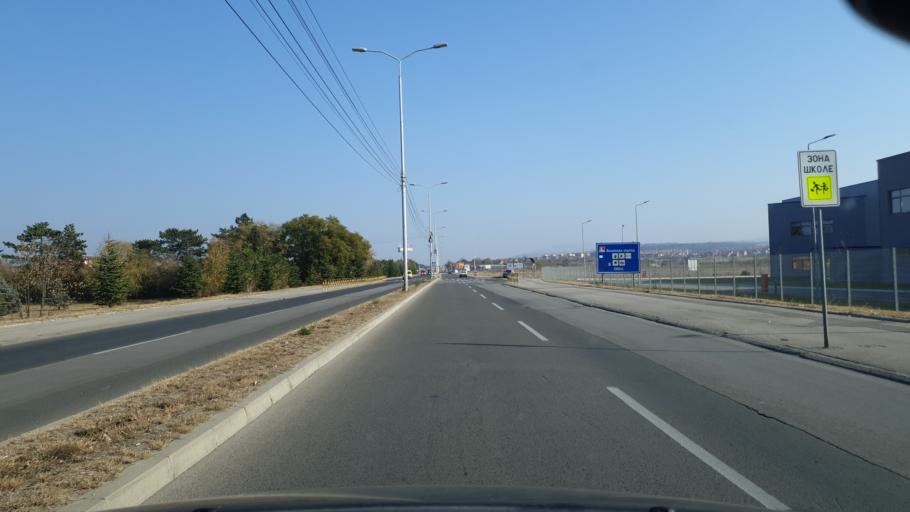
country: RS
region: Central Serbia
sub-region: Nisavski Okrug
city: Nis
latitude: 43.3177
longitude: 21.8362
